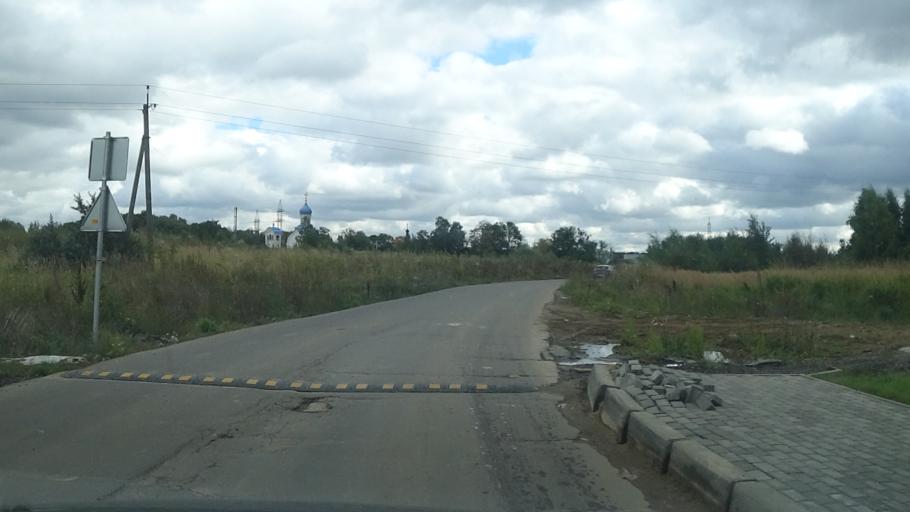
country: RU
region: Moskovskaya
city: Vostryakovo
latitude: 55.6559
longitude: 37.4305
